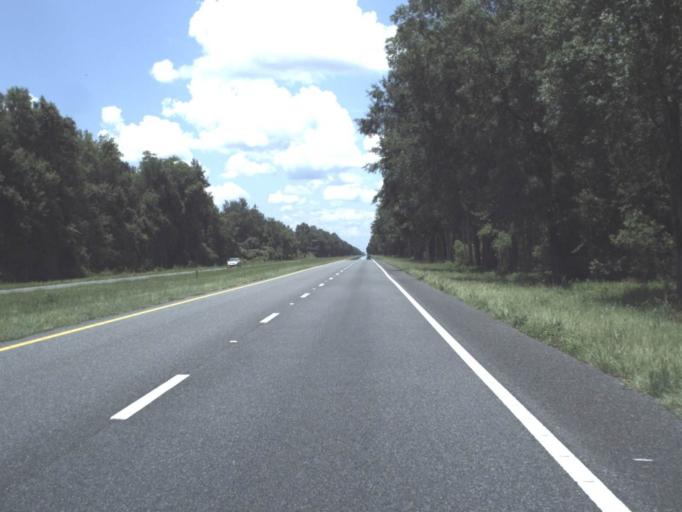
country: US
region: Florida
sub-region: Taylor County
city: Perry
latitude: 30.2148
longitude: -83.6679
